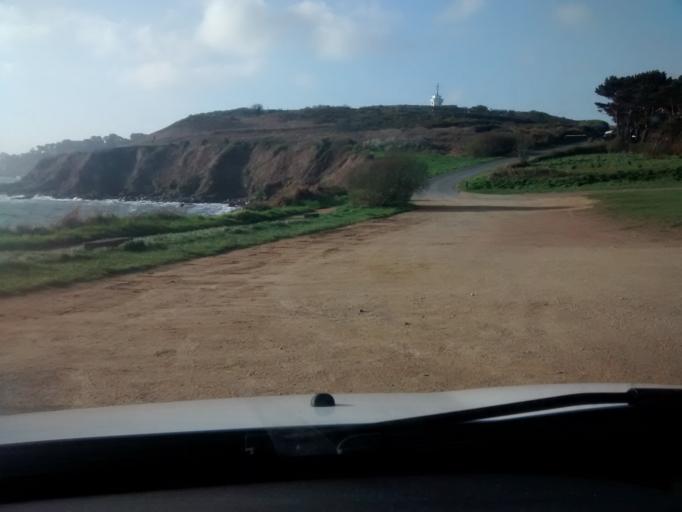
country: FR
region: Brittany
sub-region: Departement des Cotes-d'Armor
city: Tregastel
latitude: 48.8295
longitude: -3.4735
